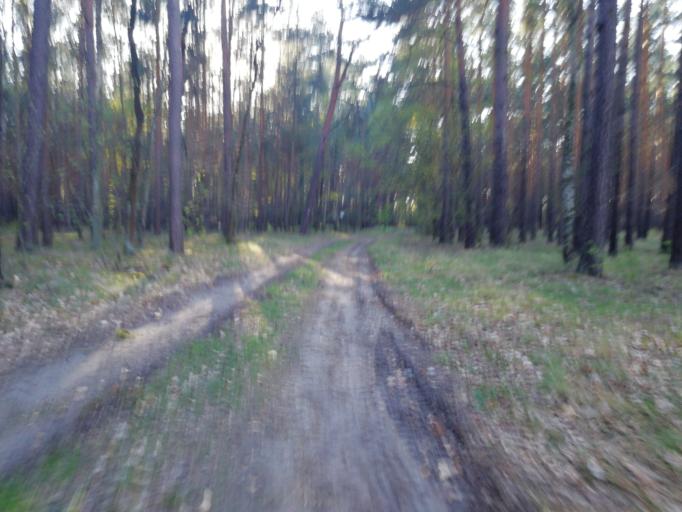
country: DE
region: Brandenburg
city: Calau
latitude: 51.7309
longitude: 14.0061
